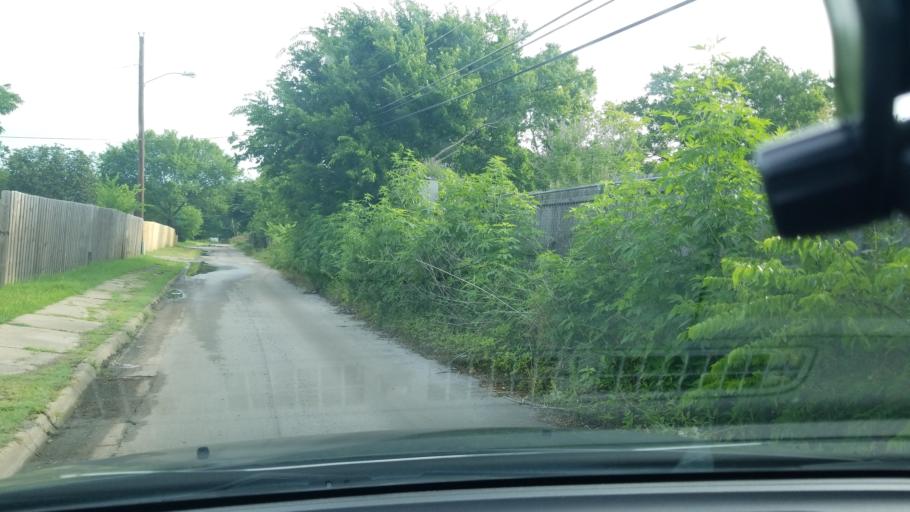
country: US
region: Texas
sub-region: Dallas County
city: Balch Springs
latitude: 32.7529
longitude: -96.6494
